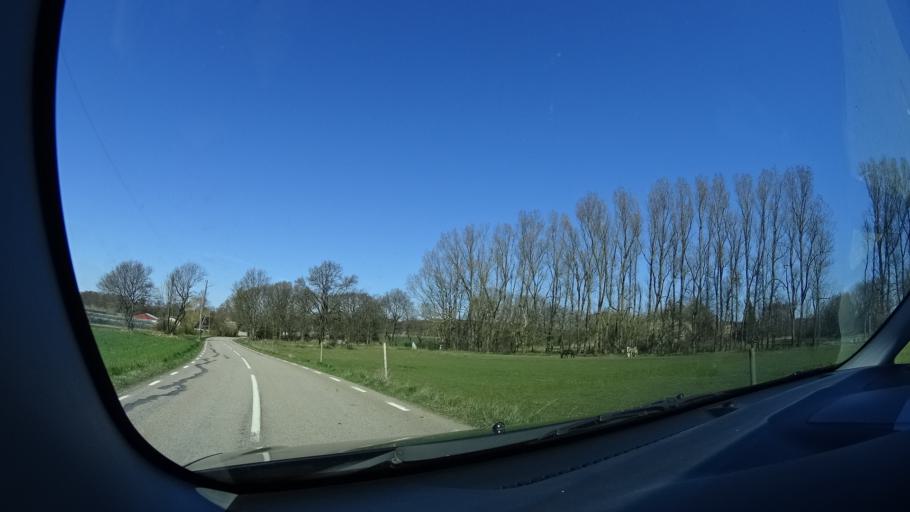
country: SE
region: Skane
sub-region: Hoganas Kommun
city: Hoganas
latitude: 56.2639
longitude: 12.5607
